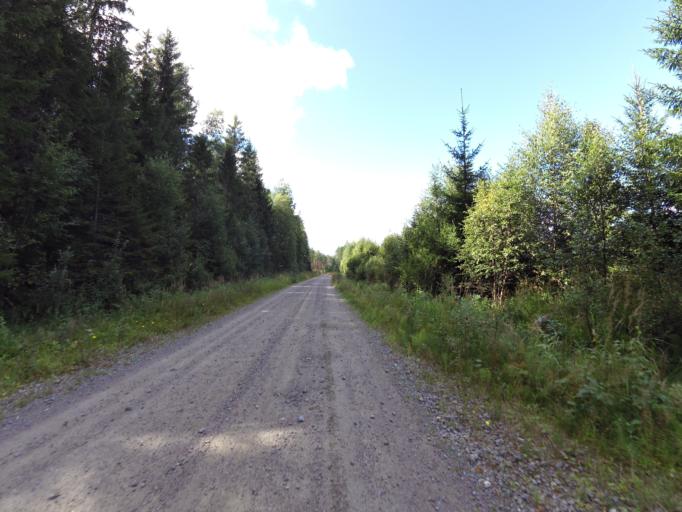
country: SE
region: Gaevleborg
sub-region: Ockelbo Kommun
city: Ockelbo
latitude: 60.8089
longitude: 16.7897
